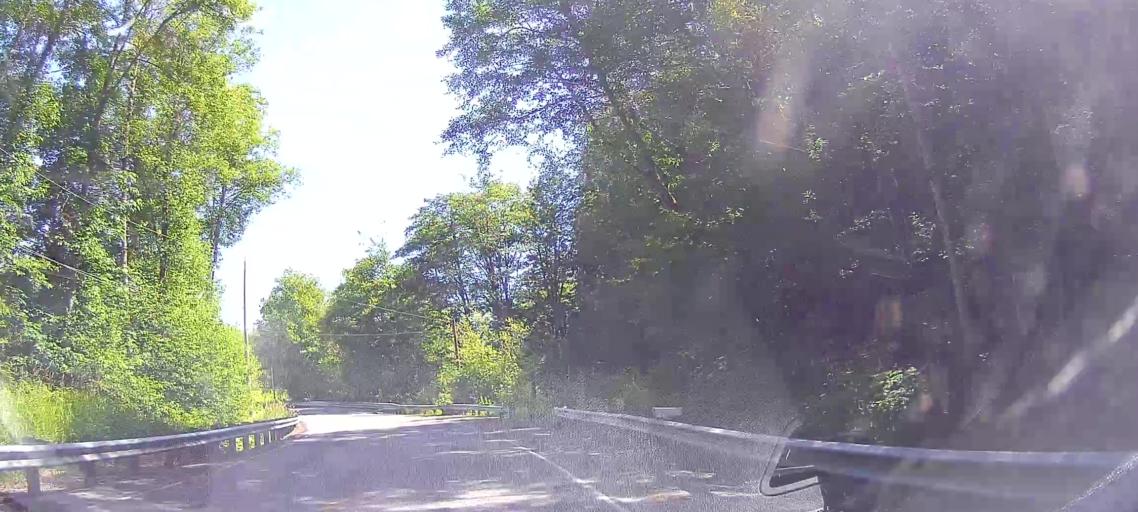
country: US
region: Washington
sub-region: Skagit County
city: Sedro-Woolley
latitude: 48.5521
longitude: -122.2961
